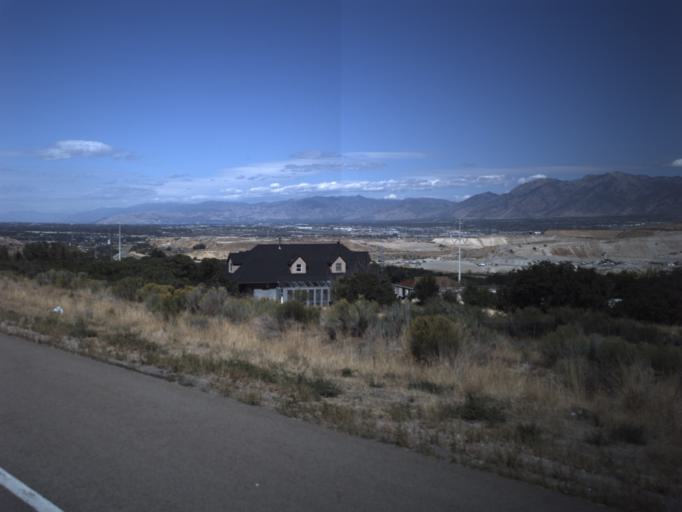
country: US
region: Utah
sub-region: Salt Lake County
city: Bluffdale
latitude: 40.4450
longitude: -111.9345
